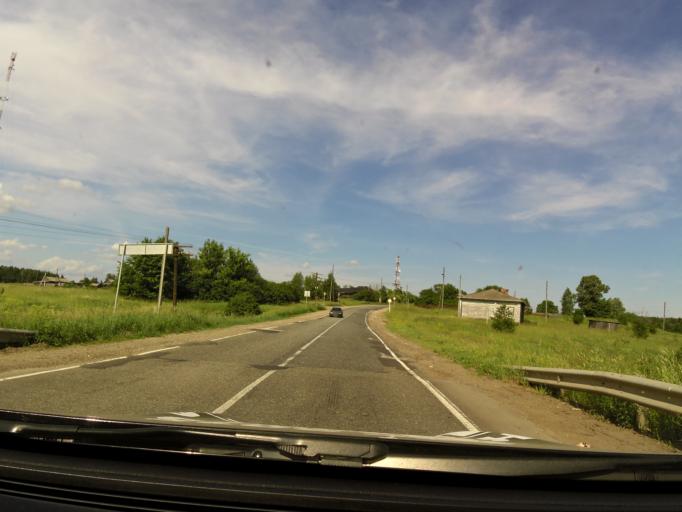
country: RU
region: Kirov
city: Belaya Kholunitsa
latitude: 58.8033
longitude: 50.5401
